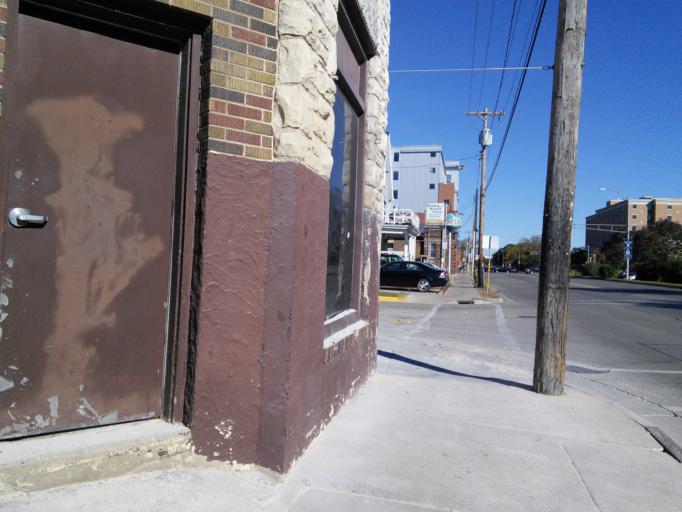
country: US
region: Wisconsin
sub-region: Dane County
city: Madison
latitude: 43.0678
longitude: -89.4027
